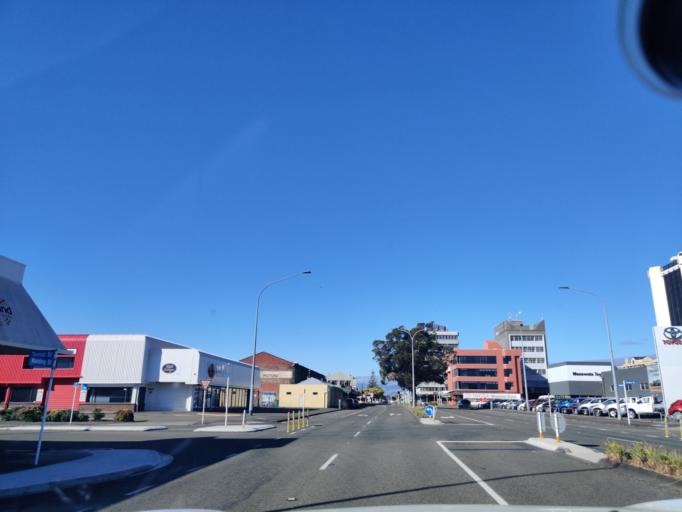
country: NZ
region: Manawatu-Wanganui
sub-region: Palmerston North City
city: Palmerston North
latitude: -40.3538
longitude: 175.6067
